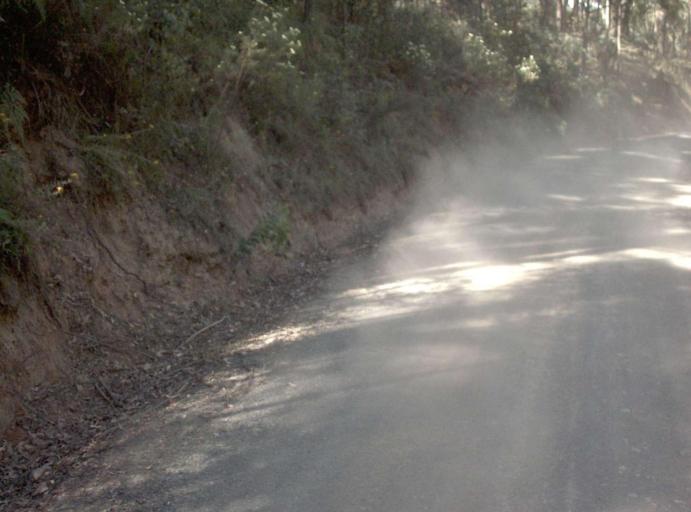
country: AU
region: New South Wales
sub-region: Bombala
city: Bombala
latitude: -37.2528
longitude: 148.7377
